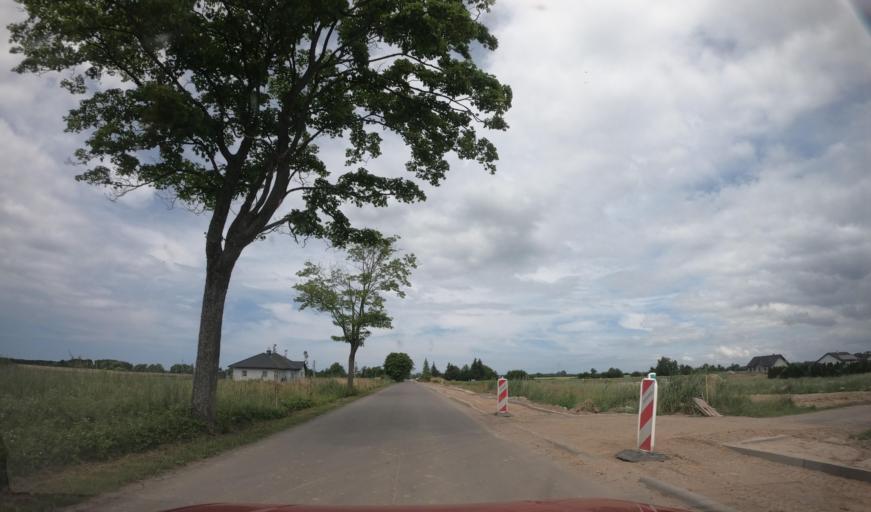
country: PL
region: West Pomeranian Voivodeship
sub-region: Powiat koszalinski
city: Mielno
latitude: 54.2282
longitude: 16.1050
